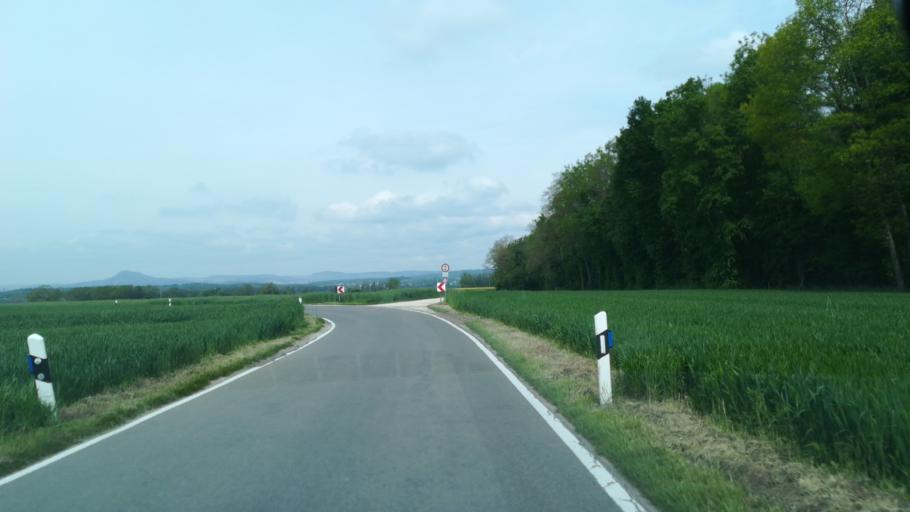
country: DE
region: Baden-Wuerttemberg
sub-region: Freiburg Region
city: Steisslingen
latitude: 47.8054
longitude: 8.9054
